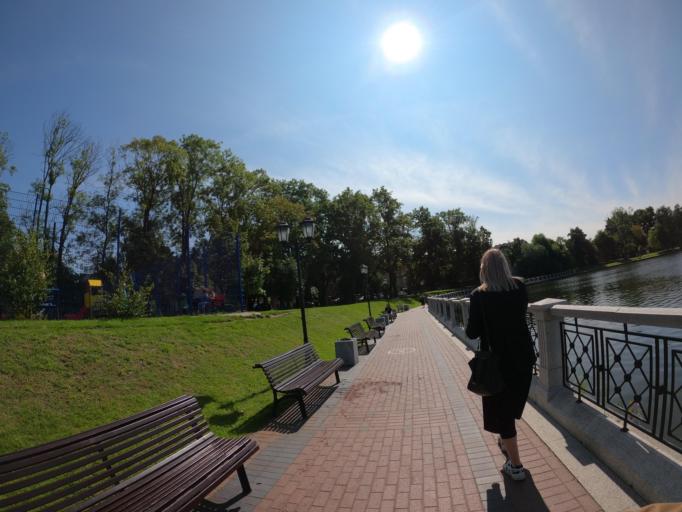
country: RU
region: Kaliningrad
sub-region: Gorod Kaliningrad
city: Kaliningrad
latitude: 54.7300
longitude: 20.5244
